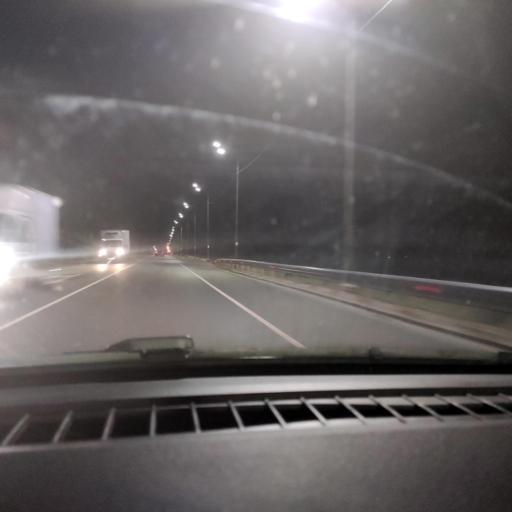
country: RU
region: Voronezj
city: Semiluki
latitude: 51.6439
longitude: 39.0191
